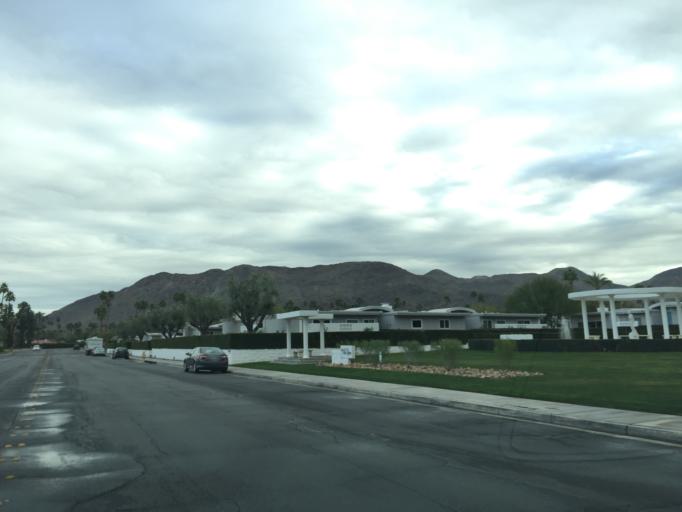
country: US
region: California
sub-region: Riverside County
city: Palm Springs
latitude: 33.7869
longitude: -116.5430
